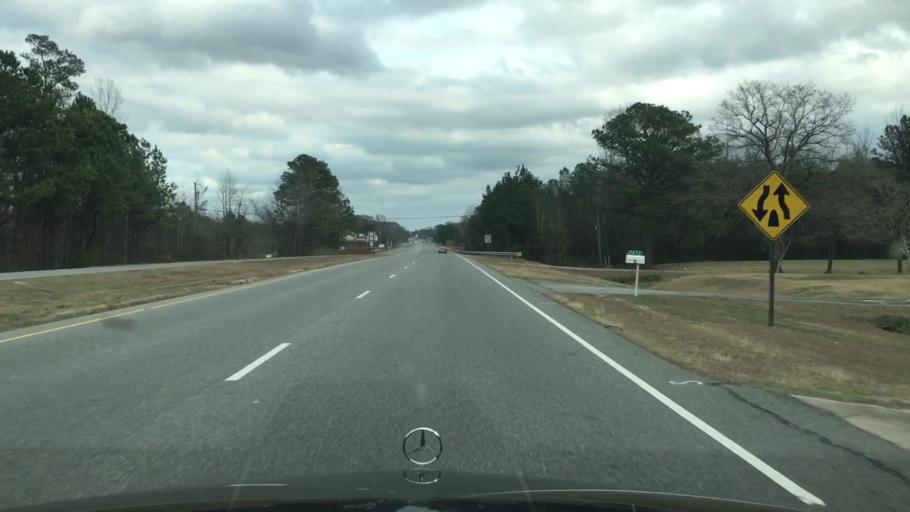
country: US
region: North Carolina
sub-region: Duplin County
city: Beulaville
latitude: 34.9293
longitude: -77.8104
